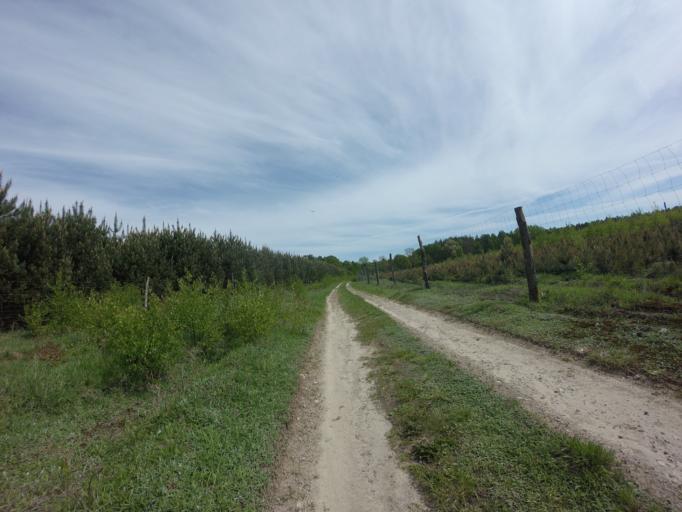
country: PL
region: West Pomeranian Voivodeship
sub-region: Powiat choszczenski
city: Recz
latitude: 53.1567
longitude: 15.5804
